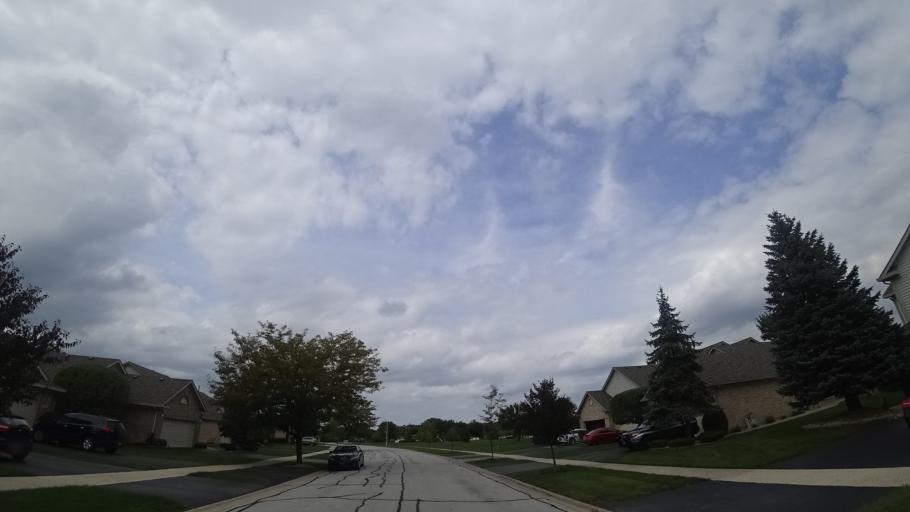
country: US
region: Illinois
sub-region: Cook County
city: Tinley Park
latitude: 41.5711
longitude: -87.8044
